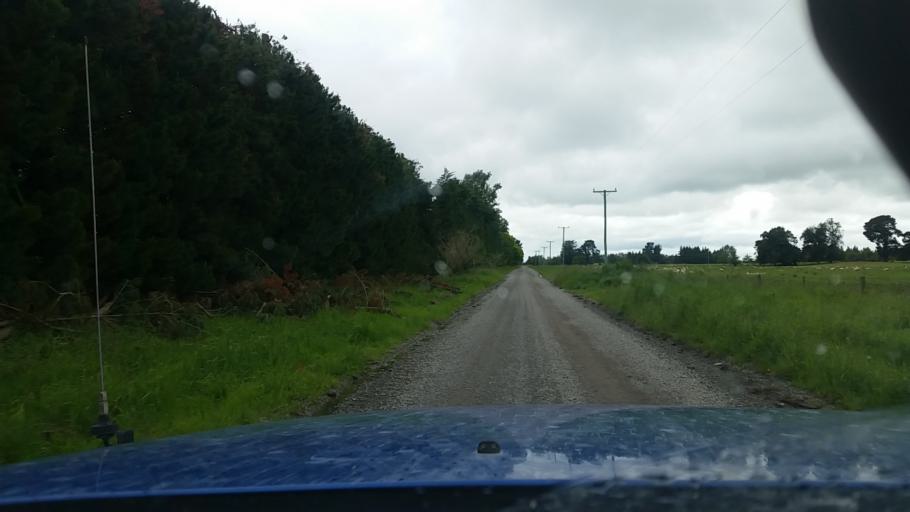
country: NZ
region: Canterbury
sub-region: Ashburton District
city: Methven
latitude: -43.6955
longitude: 171.4217
